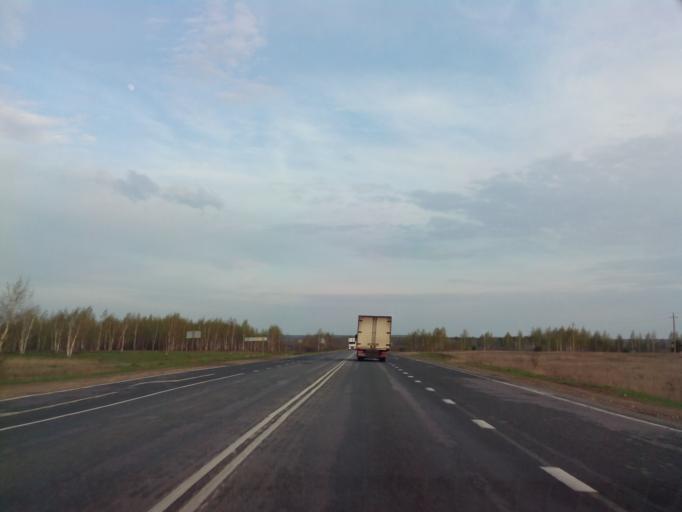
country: RU
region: Rjazan
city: Korablino
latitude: 53.7348
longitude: 39.8961
